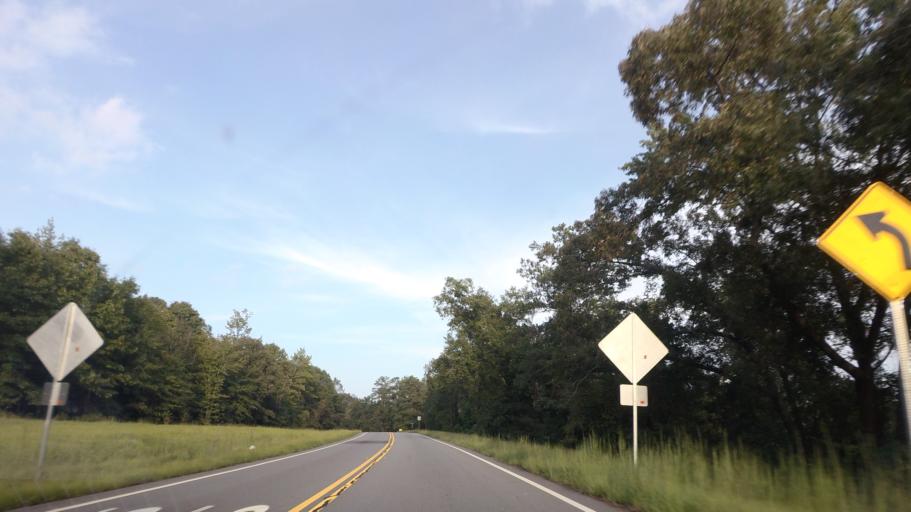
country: US
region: Georgia
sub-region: Wilkinson County
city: Gordon
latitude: 32.8586
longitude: -83.3764
